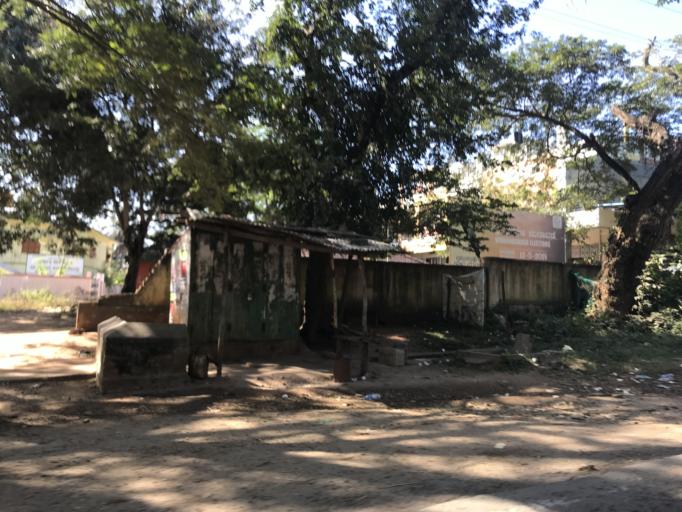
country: IN
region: Karnataka
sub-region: Mysore
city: Heggadadevankote
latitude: 12.1213
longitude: 76.4739
